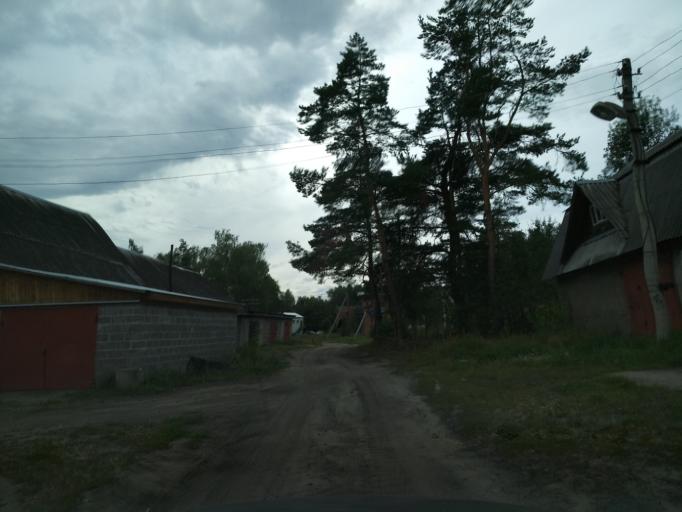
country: RU
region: Moskovskaya
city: Krasnyy Tkach
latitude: 55.3806
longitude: 39.2310
